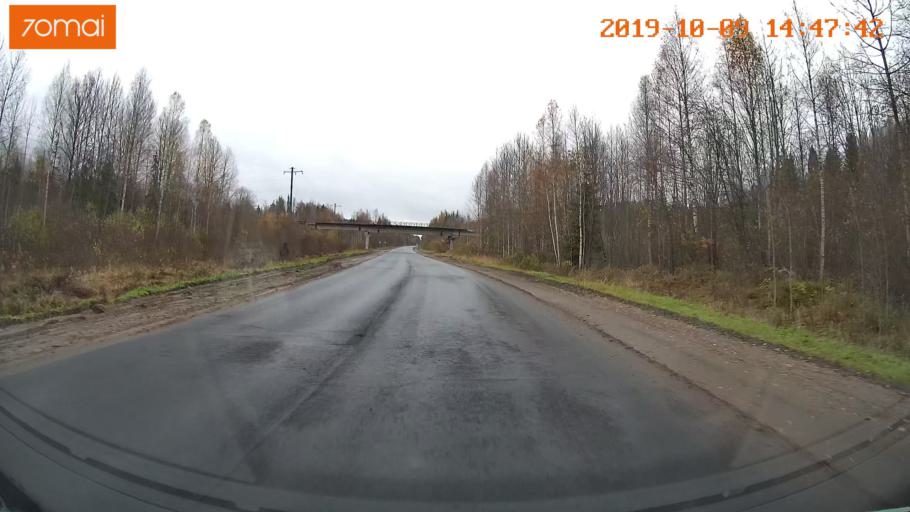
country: RU
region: Kostroma
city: Buy
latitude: 58.4147
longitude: 41.5718
